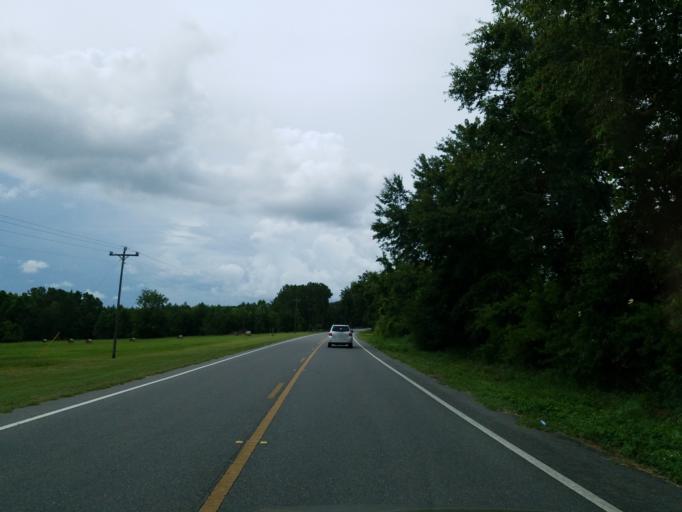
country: US
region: Florida
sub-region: Alachua County
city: High Springs
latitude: 29.9152
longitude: -82.5047
